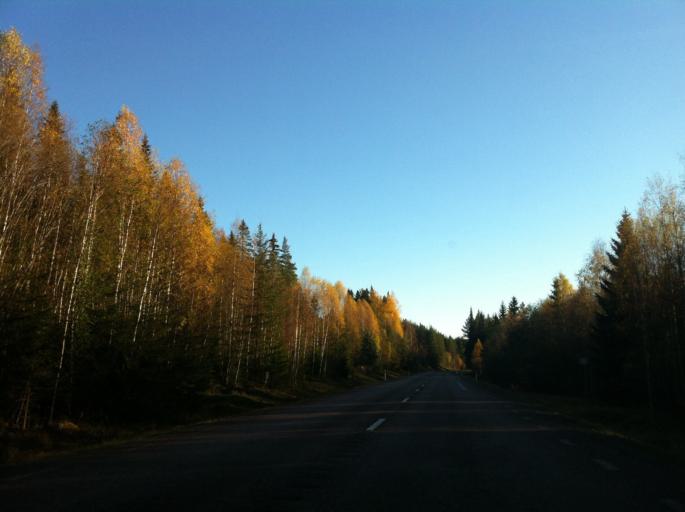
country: SE
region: Dalarna
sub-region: Faluns Kommun
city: Bjursas
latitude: 60.7793
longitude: 15.3145
